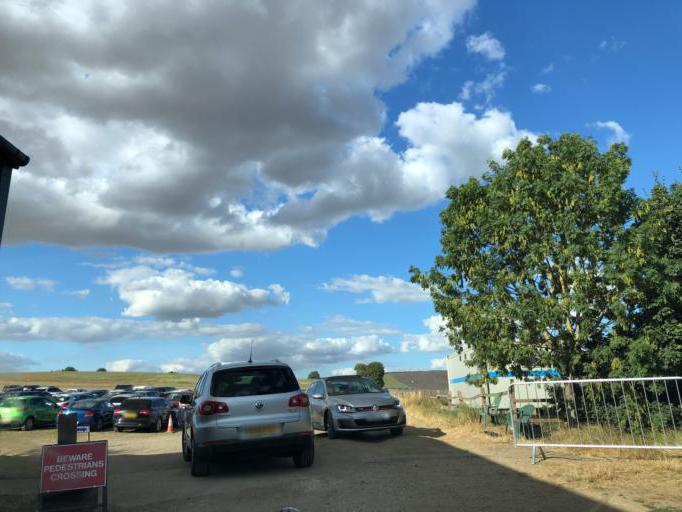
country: GB
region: England
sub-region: Central Bedfordshire
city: Arlesey
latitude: 51.9774
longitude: -0.2692
